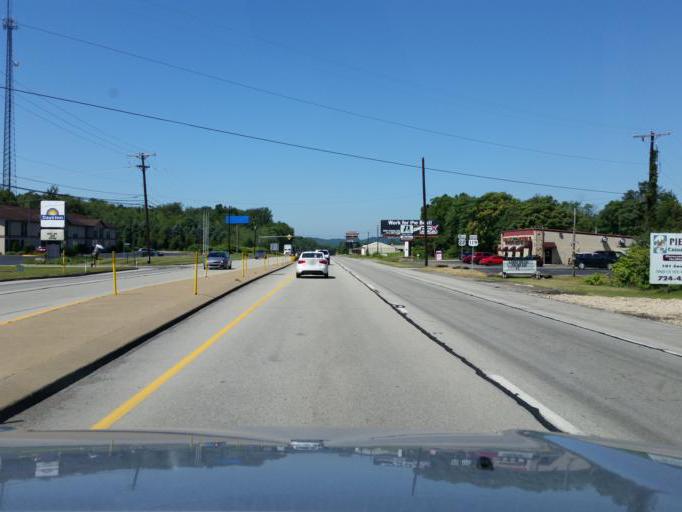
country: US
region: Pennsylvania
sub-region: Indiana County
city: Blairsville
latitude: 40.4425
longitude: -79.2367
